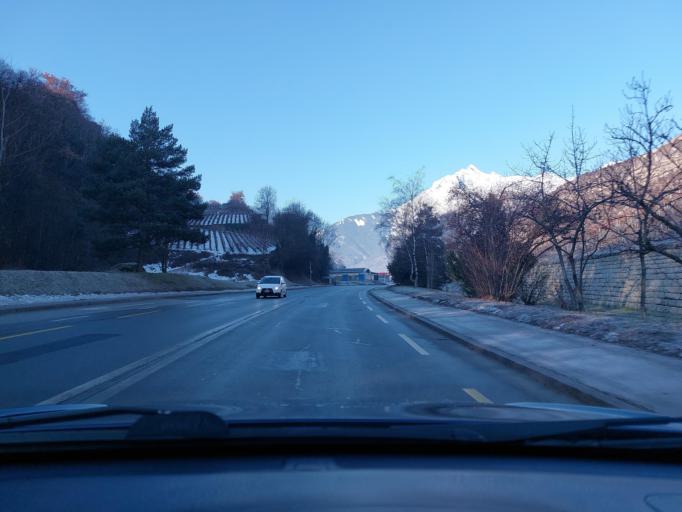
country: CH
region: Valais
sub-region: Conthey District
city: Conthey
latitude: 46.2242
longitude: 7.3300
